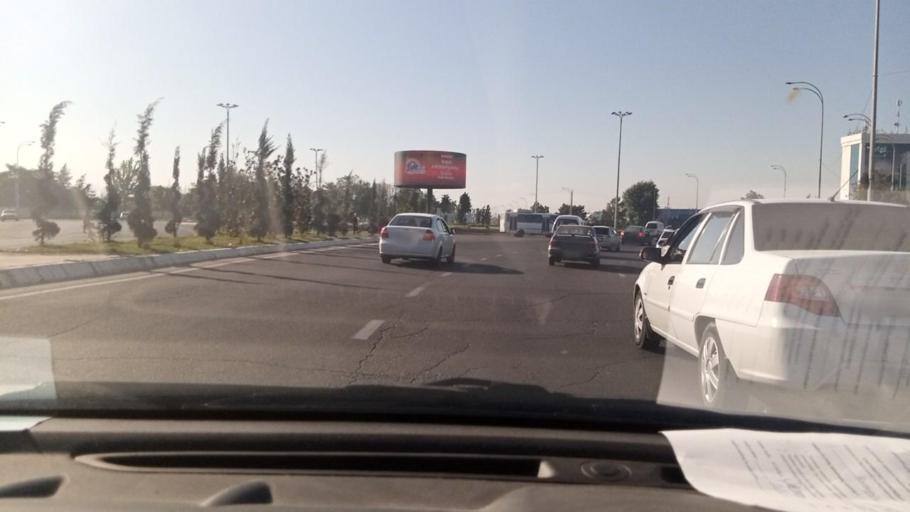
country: UZ
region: Toshkent Shahri
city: Bektemir
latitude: 41.2686
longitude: 69.3657
